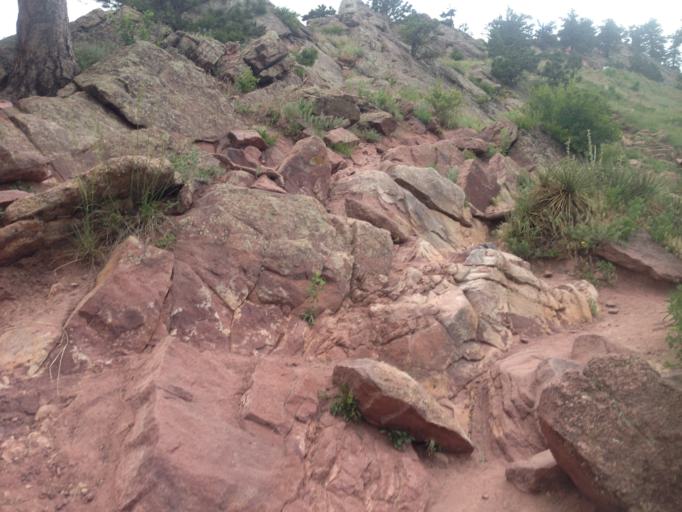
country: US
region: Colorado
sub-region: Boulder County
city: Boulder
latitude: 40.0280
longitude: -105.3017
